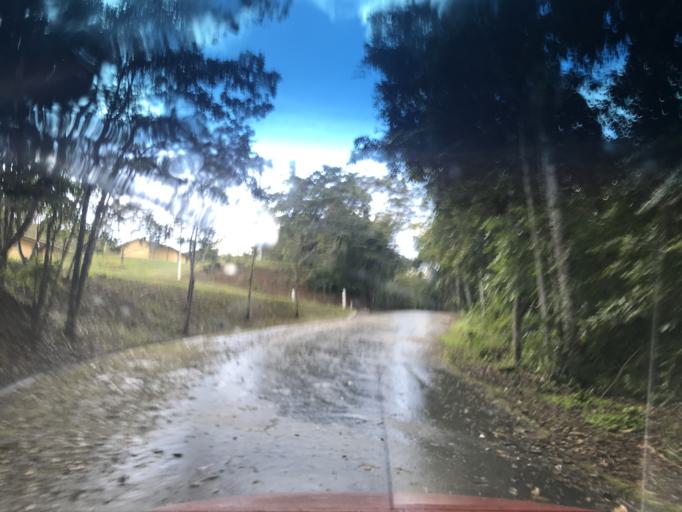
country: BR
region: Bahia
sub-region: Gandu
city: Gandu
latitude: -13.9006
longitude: -39.4597
